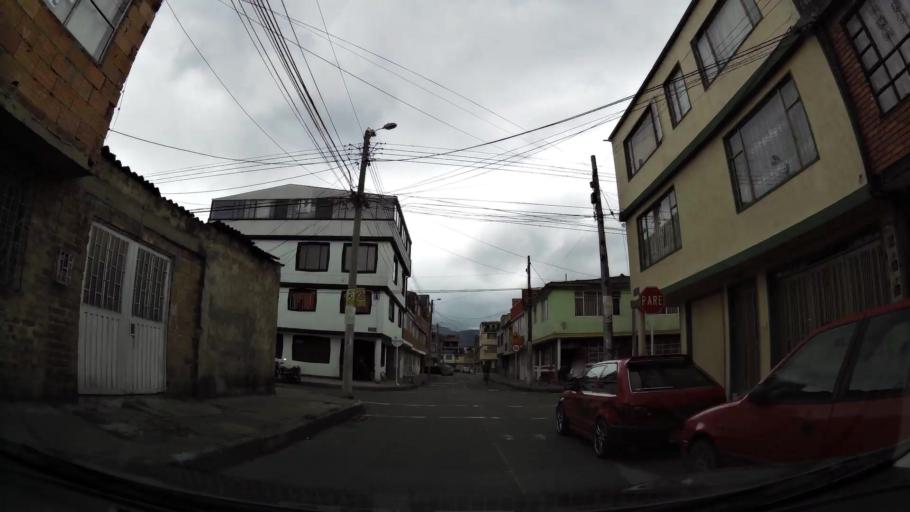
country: CO
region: Bogota D.C.
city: Bogota
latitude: 4.6751
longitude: -74.0943
